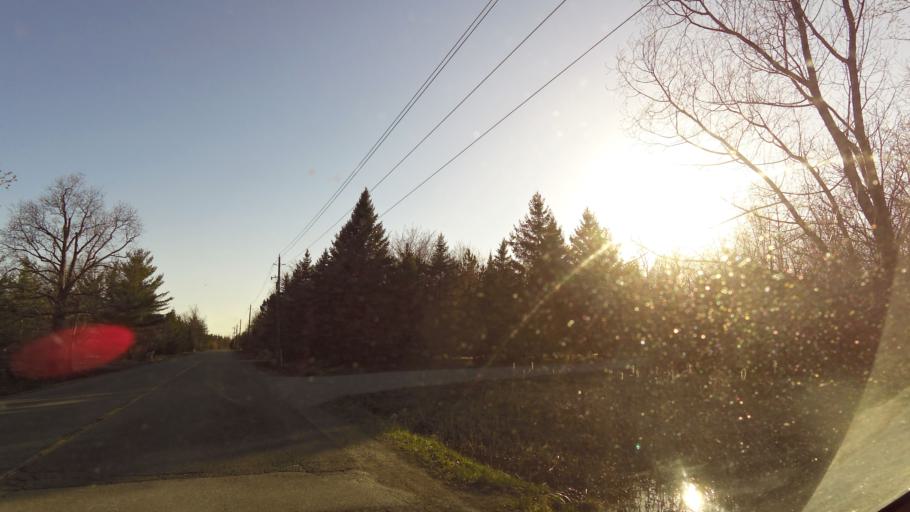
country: CA
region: Ontario
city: Brampton
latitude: 43.8522
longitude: -79.7400
